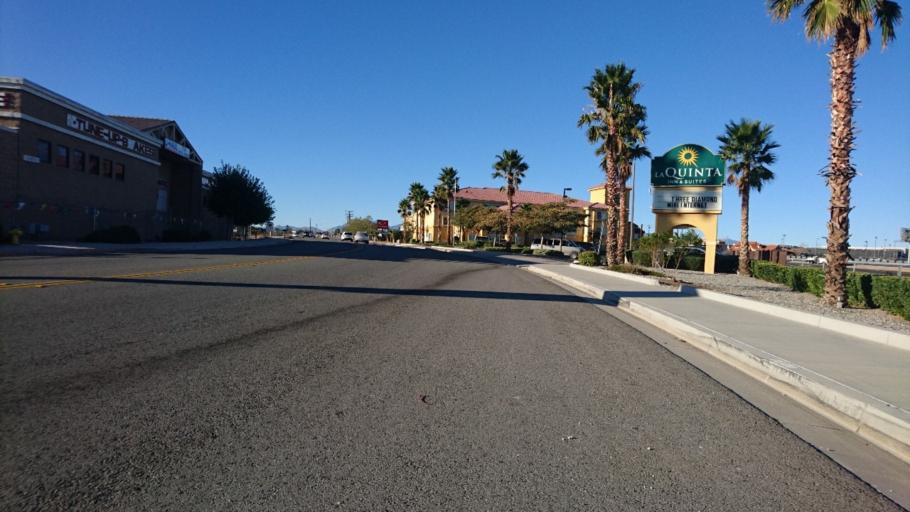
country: US
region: California
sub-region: San Bernardino County
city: Mountain View Acres
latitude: 34.4692
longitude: -117.3453
